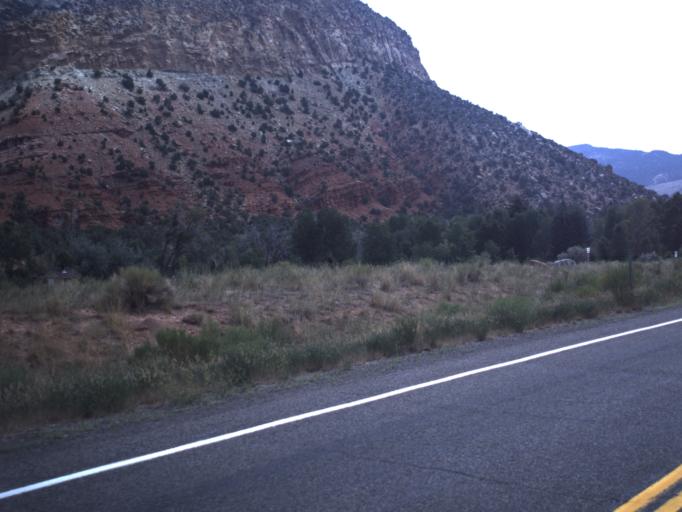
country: US
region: Utah
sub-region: Daggett County
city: Manila
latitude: 40.9238
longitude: -109.7097
